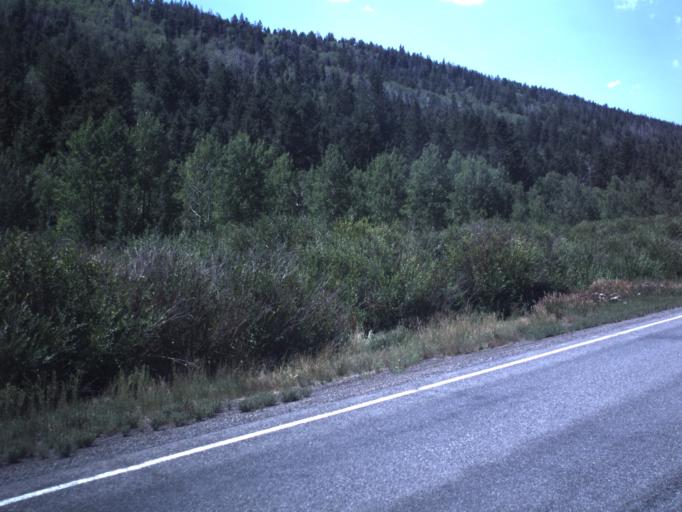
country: US
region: Utah
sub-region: Carbon County
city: Helper
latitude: 39.8571
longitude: -111.0682
